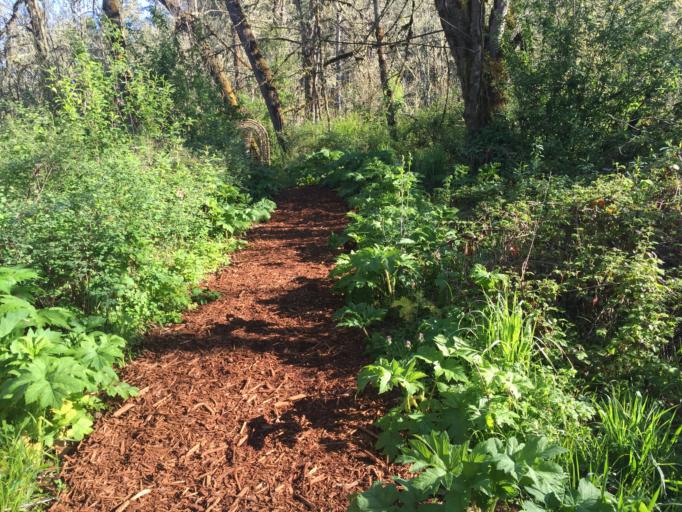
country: US
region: Oregon
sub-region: Lane County
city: Springfield
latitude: 44.0017
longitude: -122.9797
